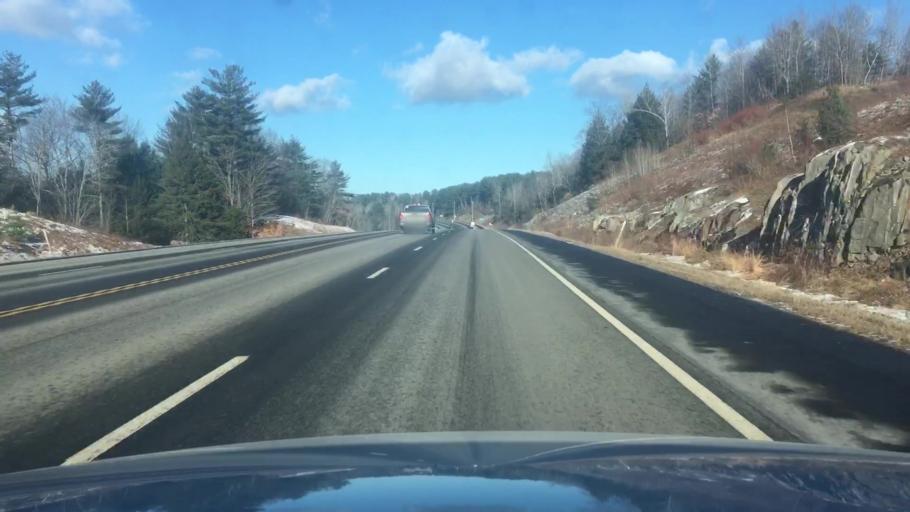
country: US
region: Maine
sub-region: Kennebec County
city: Augusta
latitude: 44.3399
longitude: -69.7675
